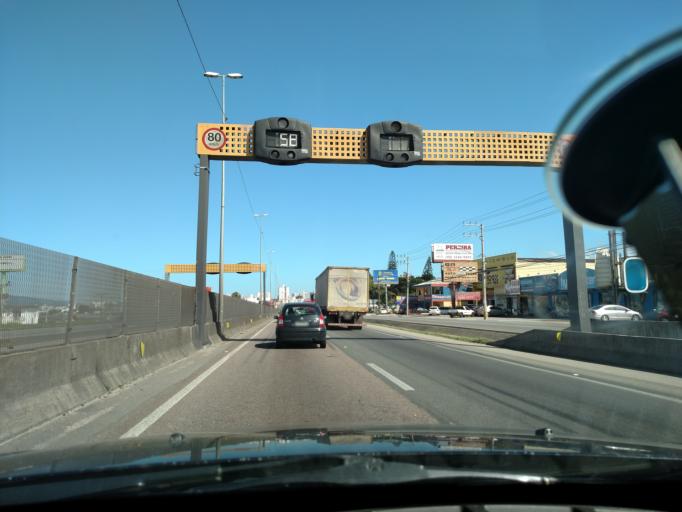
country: BR
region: Santa Catarina
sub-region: Sao Jose
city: Campinas
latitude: -27.5584
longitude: -48.6183
